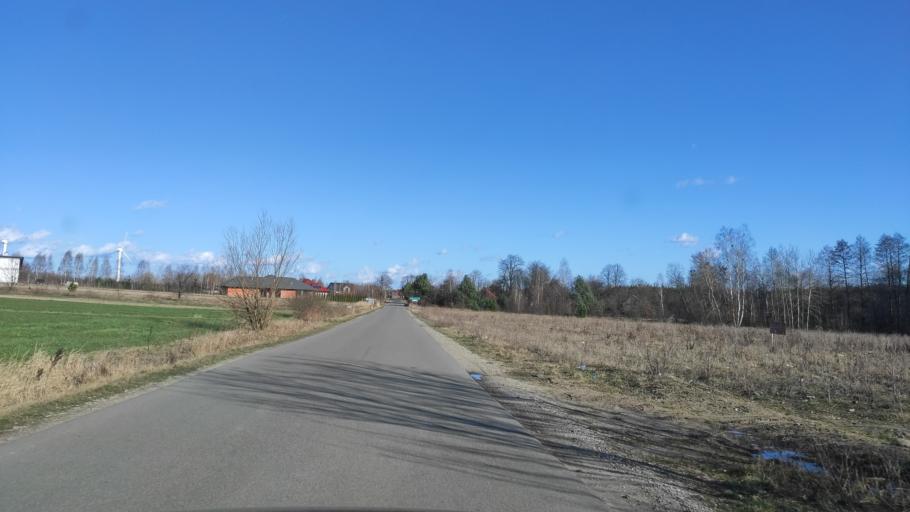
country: PL
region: Masovian Voivodeship
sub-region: Powiat radomski
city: Jastrzebia
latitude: 51.4530
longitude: 21.2417
